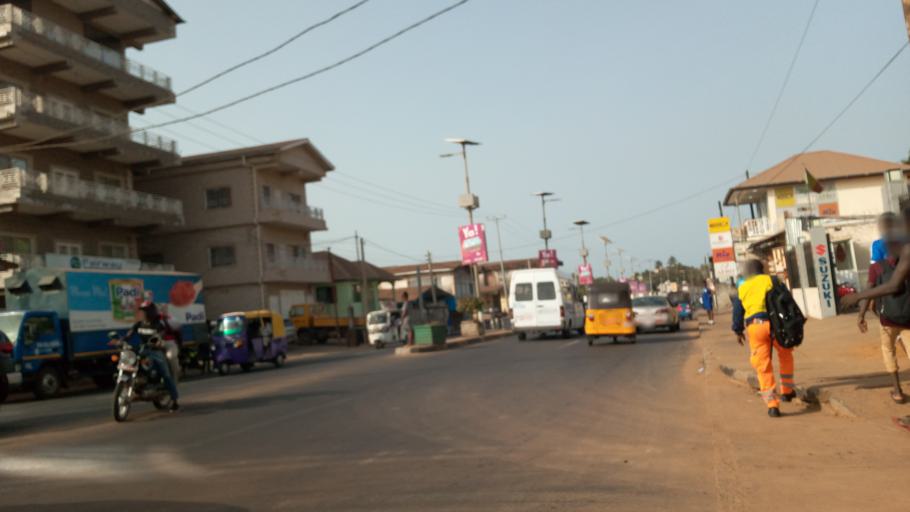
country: SL
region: Western Area
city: Freetown
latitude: 8.4826
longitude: -13.2688
